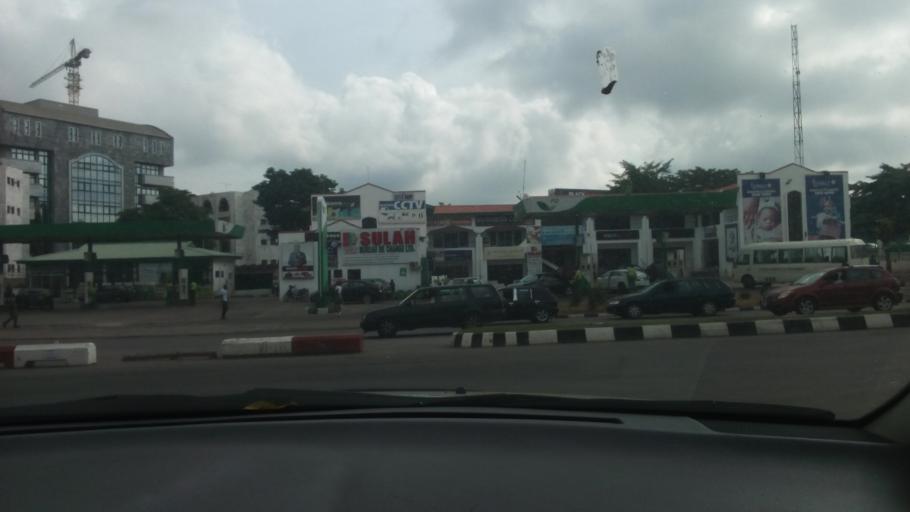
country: NG
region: Abuja Federal Capital Territory
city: Abuja
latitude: 9.0778
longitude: 7.4961
